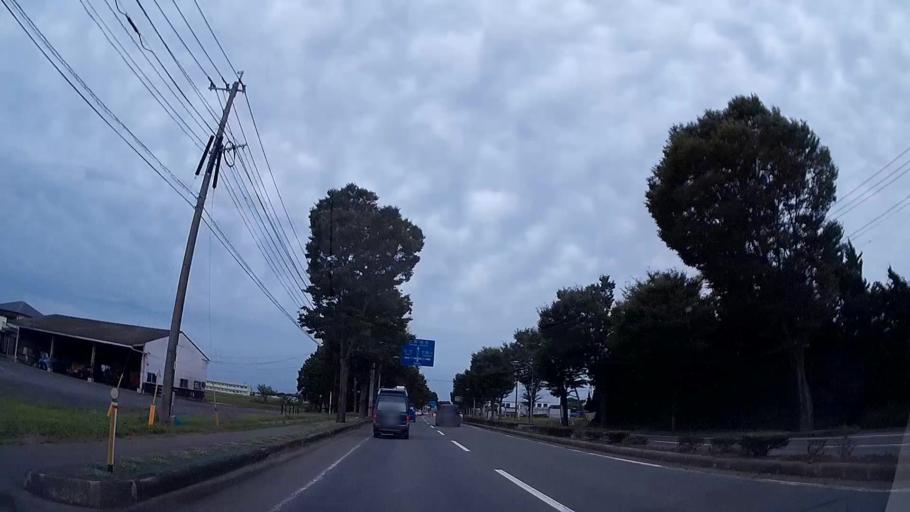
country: JP
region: Kumamoto
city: Ozu
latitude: 32.9090
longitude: 130.8464
